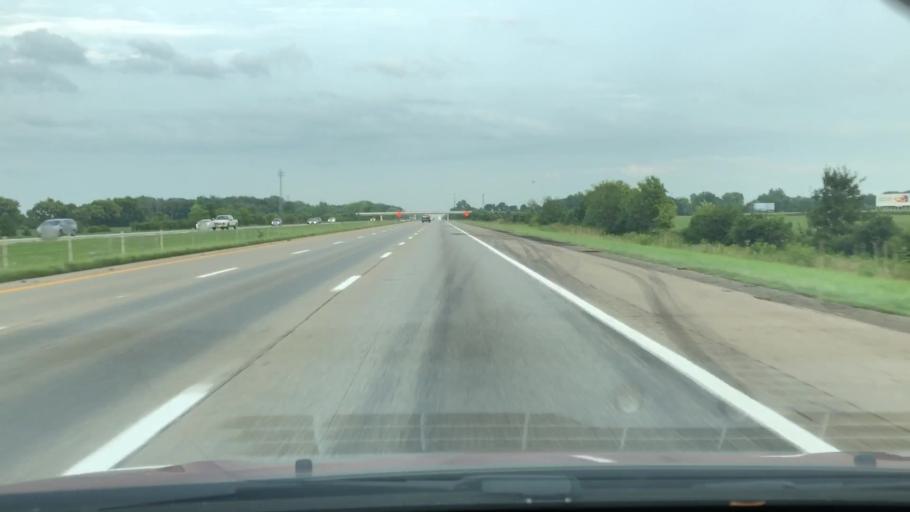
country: US
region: Ohio
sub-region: Franklin County
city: Lake Darby
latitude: 39.9796
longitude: -83.2147
